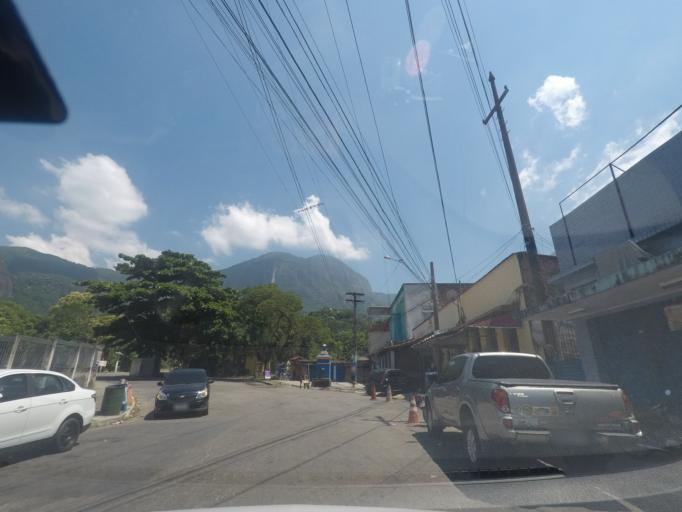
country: BR
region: Rio de Janeiro
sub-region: Petropolis
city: Petropolis
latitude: -22.5704
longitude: -43.1844
